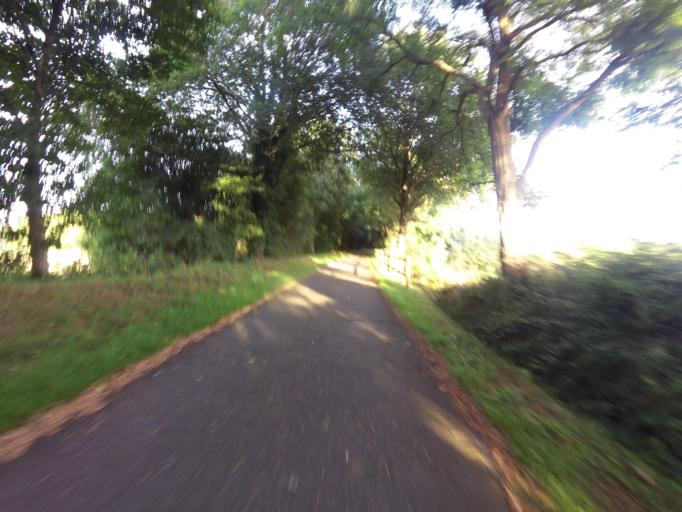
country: FR
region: Brittany
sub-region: Departement du Morbihan
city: Malestroit
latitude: 47.8143
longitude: -2.4092
